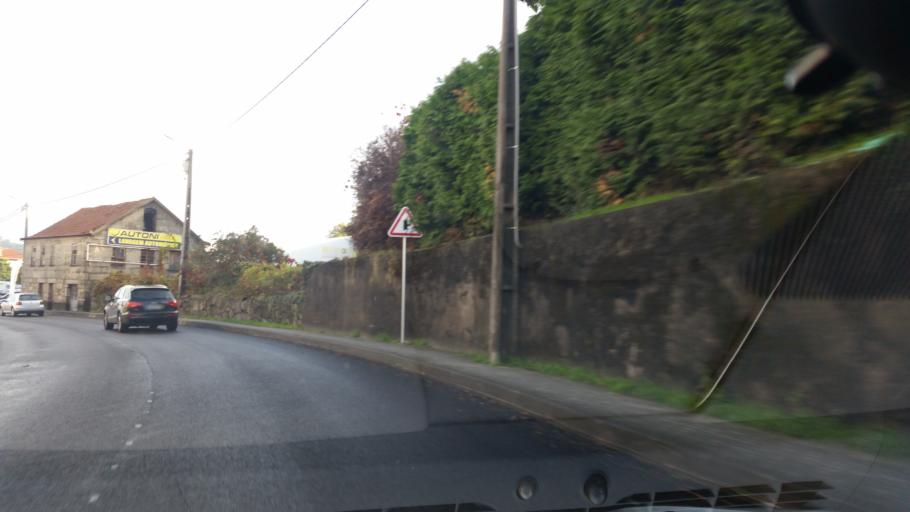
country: PT
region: Porto
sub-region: Santo Tirso
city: Negrelos
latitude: 41.3561
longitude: -8.4033
